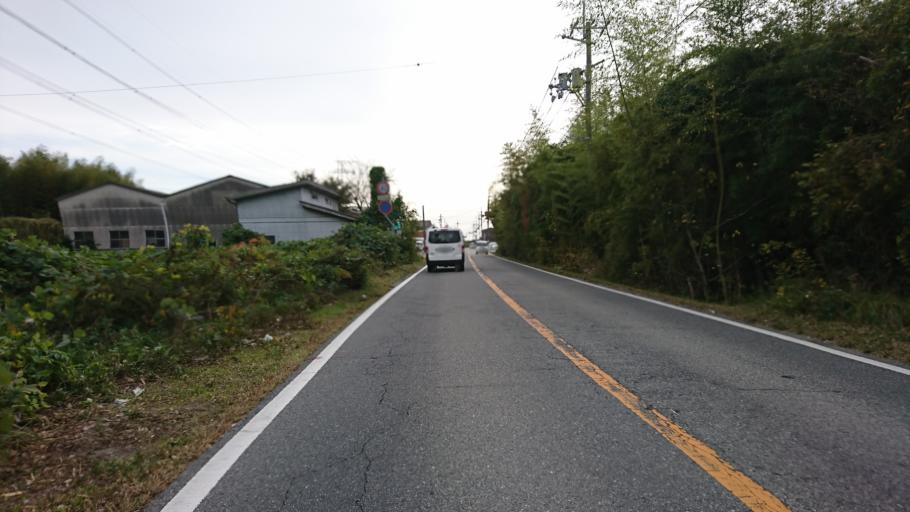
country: JP
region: Hyogo
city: Ono
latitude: 34.8011
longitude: 134.9250
